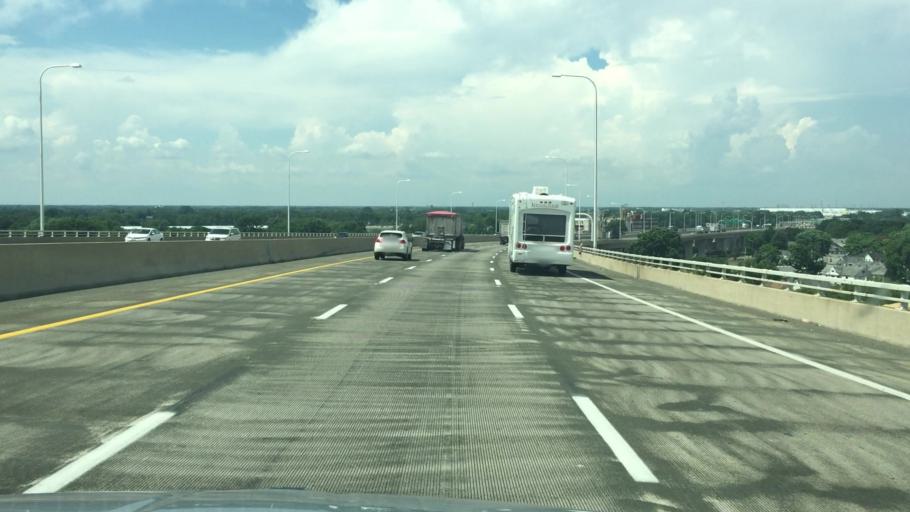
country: US
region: Ohio
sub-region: Lucas County
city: Oregon
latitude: 41.6635
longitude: -83.5133
